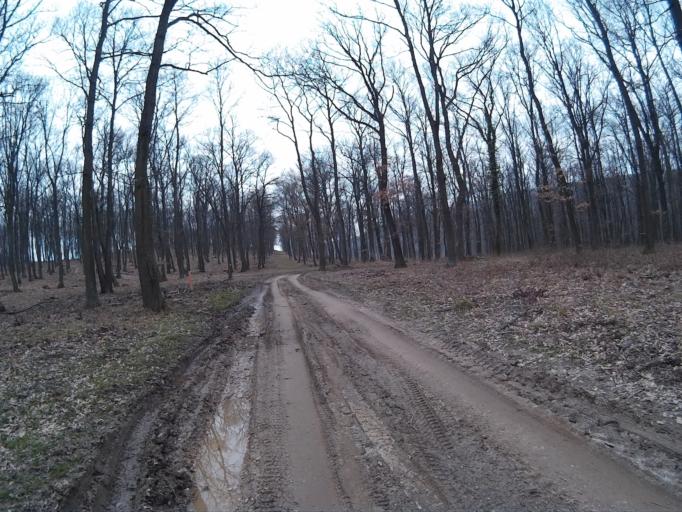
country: HU
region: Veszprem
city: Zirc
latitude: 47.1846
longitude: 17.8988
